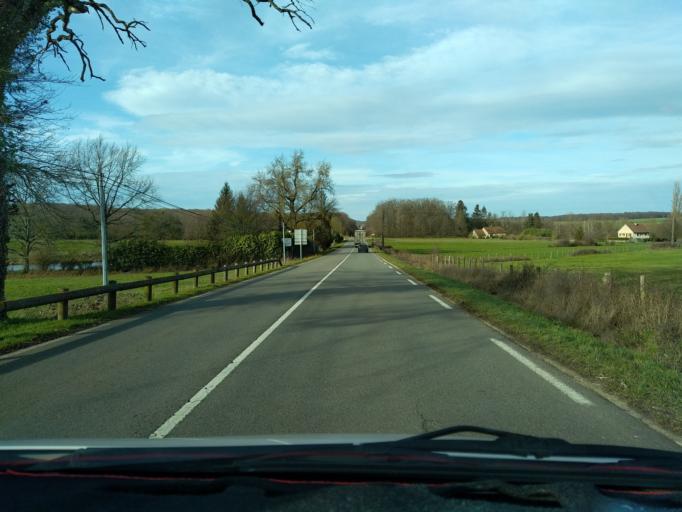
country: FR
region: Franche-Comte
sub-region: Departement de la Haute-Saone
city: Gray
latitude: 47.3745
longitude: 5.6646
